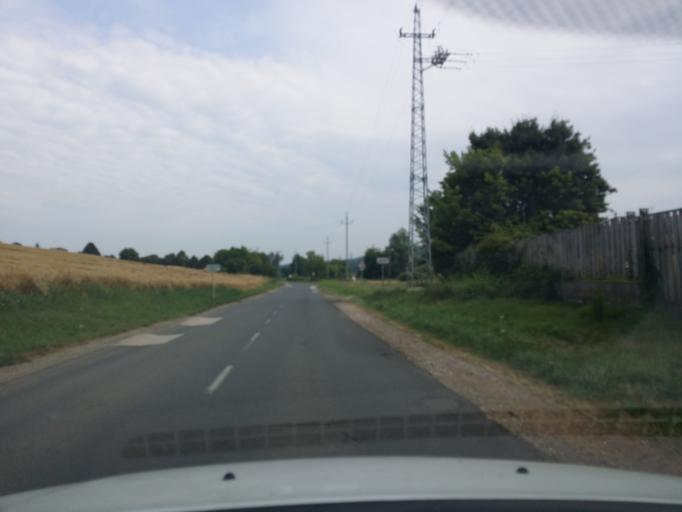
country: HU
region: Pest
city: Acsa
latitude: 47.8046
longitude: 19.3863
